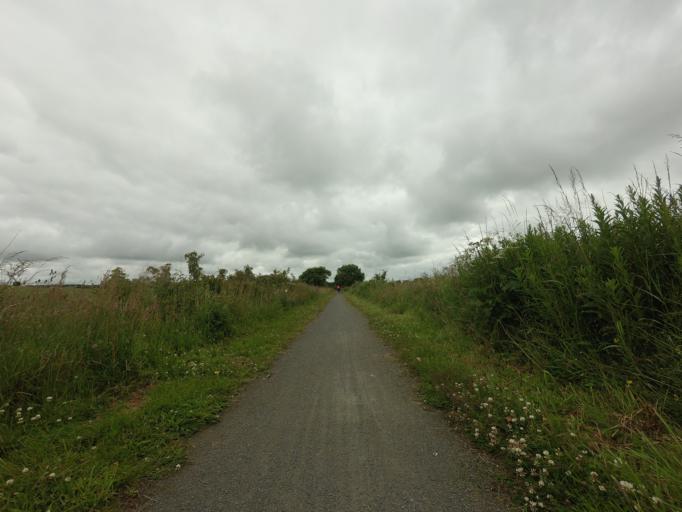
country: GB
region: Scotland
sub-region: Aberdeenshire
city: Ellon
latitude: 57.4703
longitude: -2.1213
